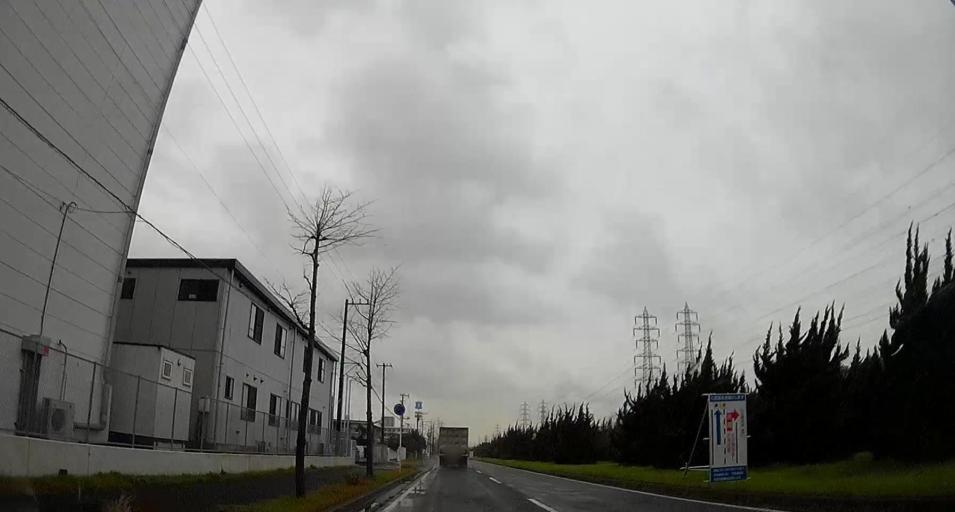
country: JP
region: Chiba
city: Ichihara
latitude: 35.4821
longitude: 140.0368
